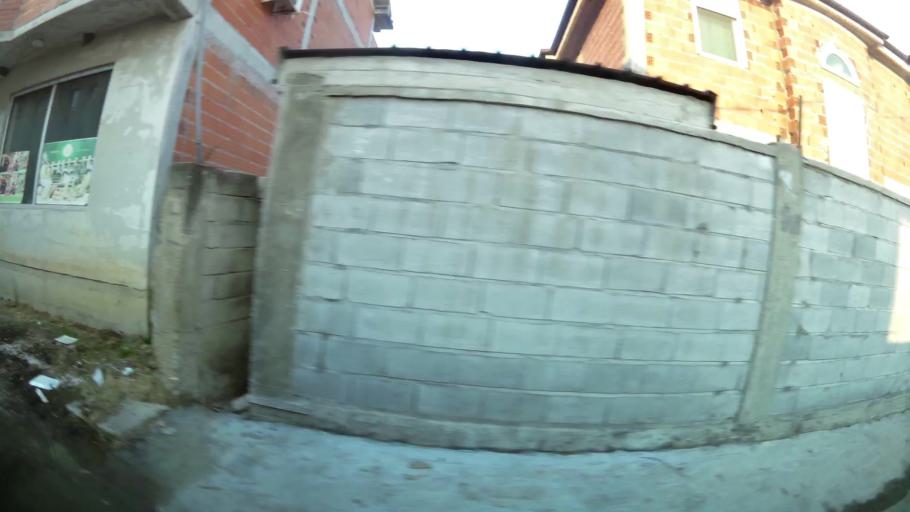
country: MK
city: Creshevo
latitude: 42.0180
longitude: 21.5206
